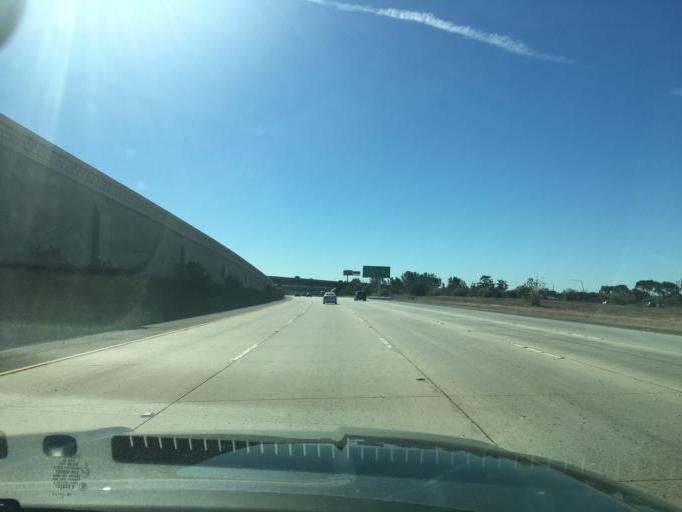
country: US
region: California
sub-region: San Diego County
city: Poway
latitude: 32.8601
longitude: -117.1130
